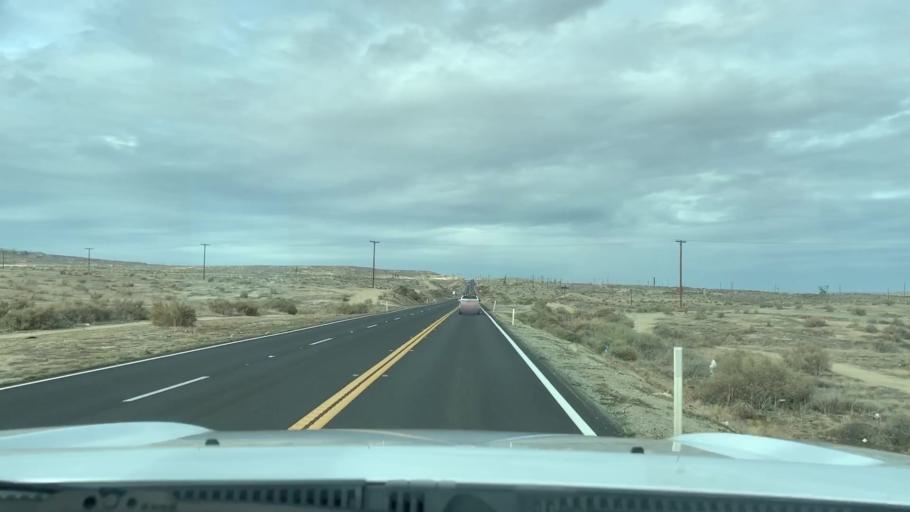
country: US
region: California
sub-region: Kern County
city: South Taft
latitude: 35.1071
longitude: -119.4217
